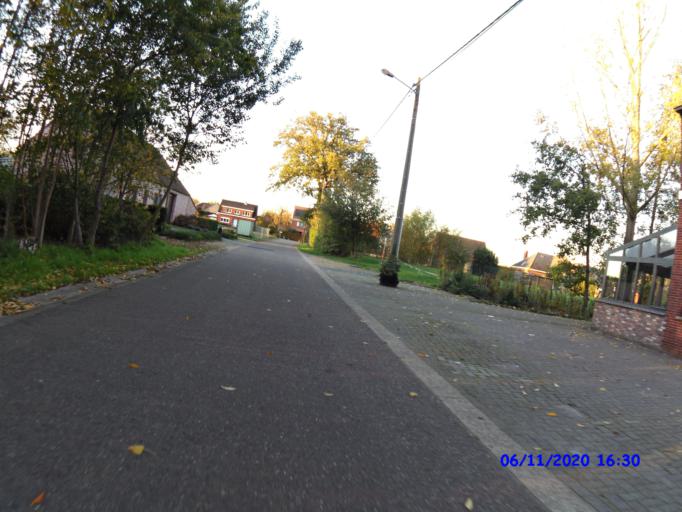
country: BE
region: Flanders
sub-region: Provincie Antwerpen
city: Mol
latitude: 51.1883
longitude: 5.0602
